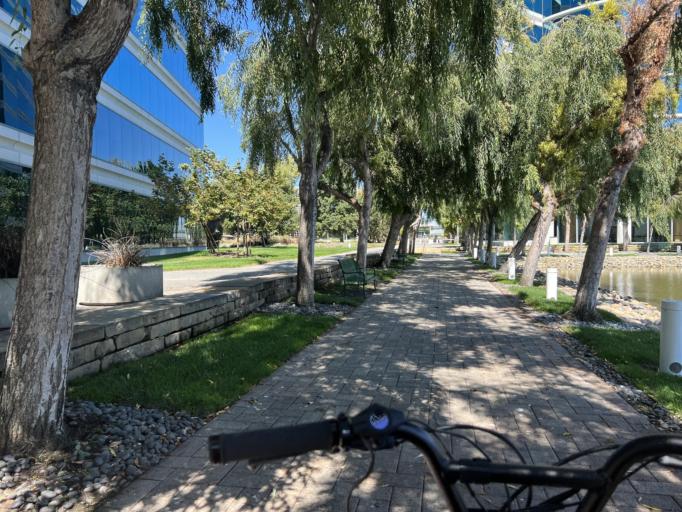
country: US
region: California
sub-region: San Mateo County
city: Belmont
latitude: 37.5299
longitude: -122.2651
